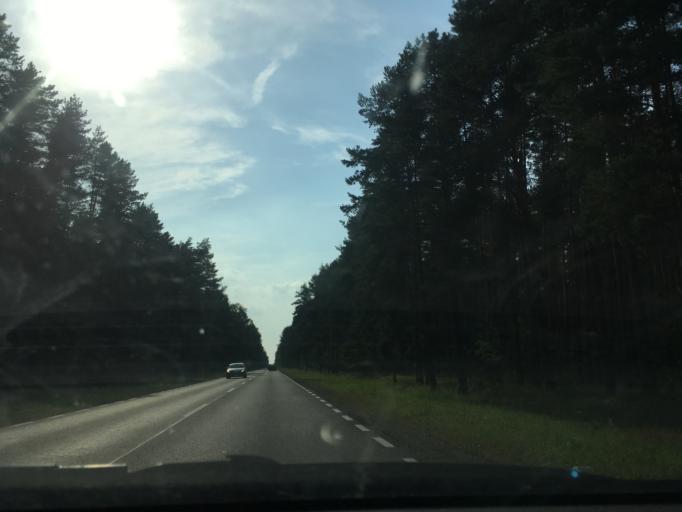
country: PL
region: Podlasie
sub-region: Powiat bialostocki
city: Suprasl
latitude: 53.1255
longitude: 23.3257
